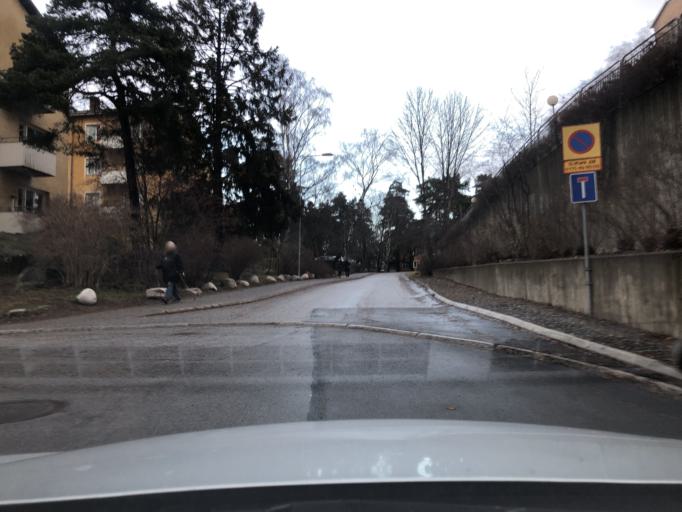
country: SE
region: Stockholm
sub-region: Stockholms Kommun
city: Arsta
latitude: 59.2987
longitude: 18.0509
